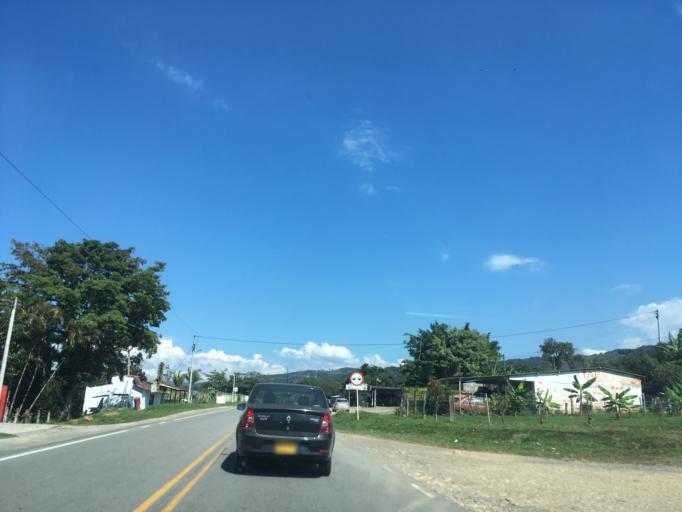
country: CO
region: Santander
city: Suaita
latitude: 6.0749
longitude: -73.4056
